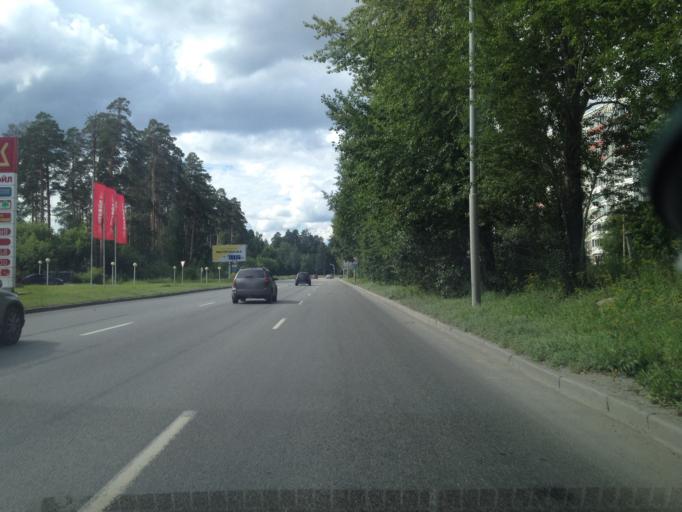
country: RU
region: Sverdlovsk
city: Sovkhoznyy
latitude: 56.8022
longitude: 60.5458
